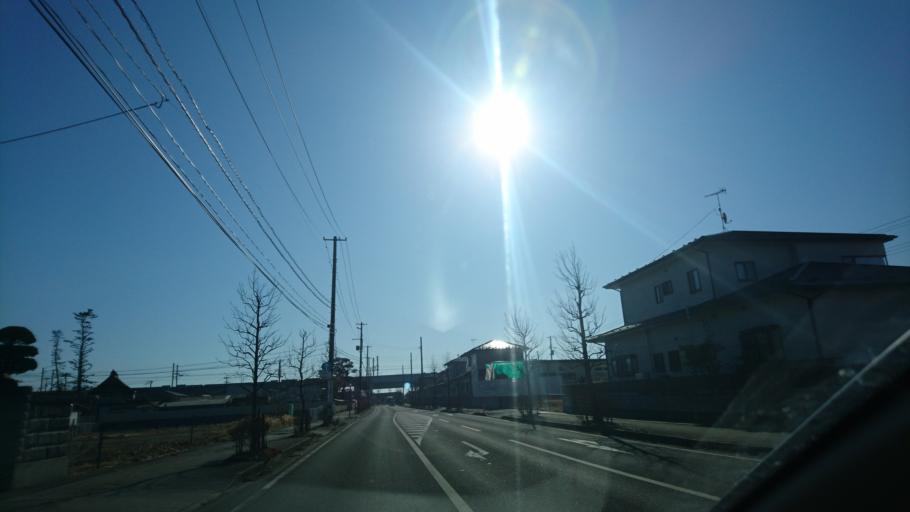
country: JP
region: Miyagi
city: Furukawa
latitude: 38.5874
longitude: 140.9701
